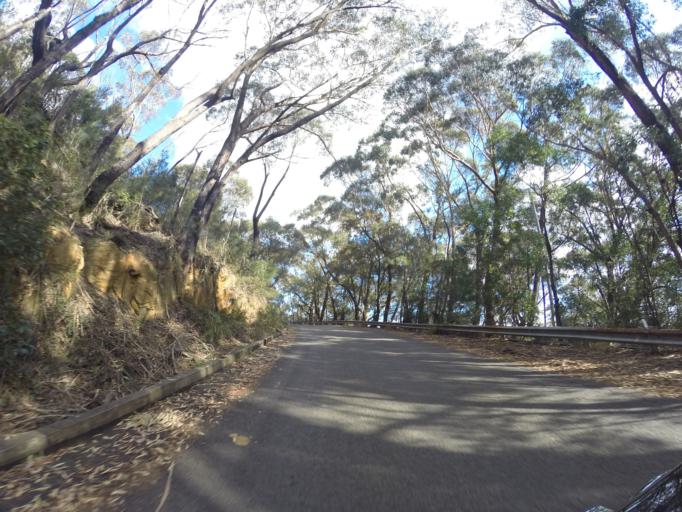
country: AU
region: New South Wales
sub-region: Wollongong
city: Mount Keira
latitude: -34.3998
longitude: 150.8550
